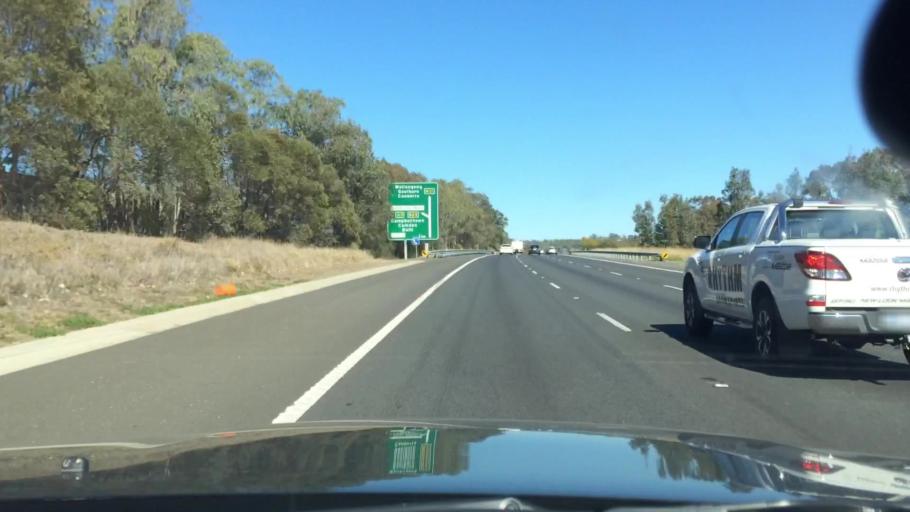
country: AU
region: New South Wales
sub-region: Campbelltown Municipality
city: Campbelltown
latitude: -34.0525
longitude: 150.8104
